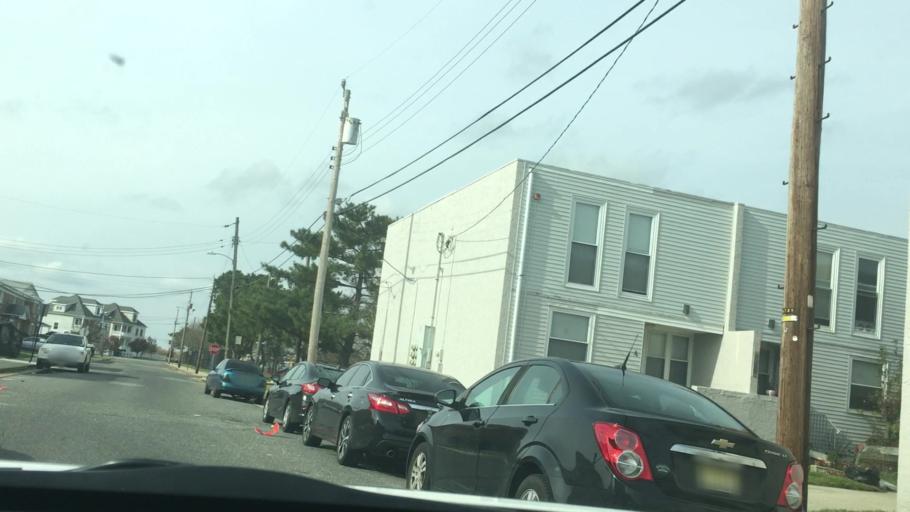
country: US
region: New Jersey
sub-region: Atlantic County
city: Atlantic City
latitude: 39.3717
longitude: -74.4540
